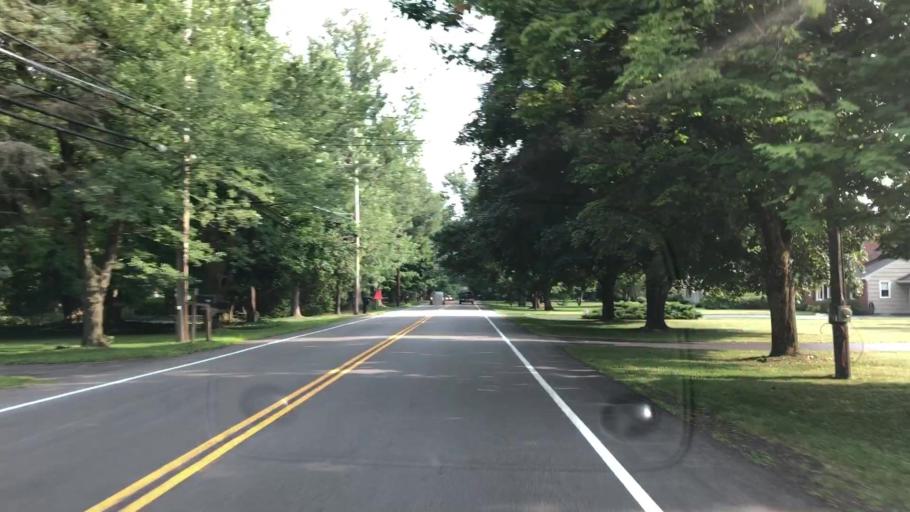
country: US
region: New York
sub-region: Erie County
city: Billington Heights
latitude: 42.7797
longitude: -78.6208
